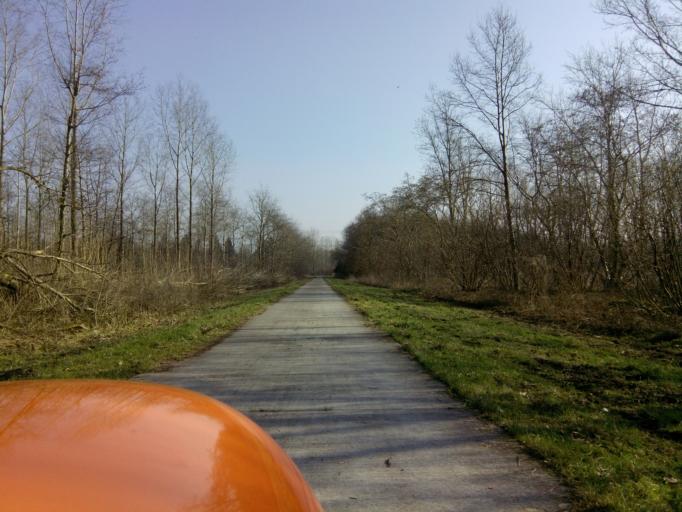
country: NL
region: Flevoland
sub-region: Gemeente Zeewolde
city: Zeewolde
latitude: 52.3388
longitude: 5.4534
